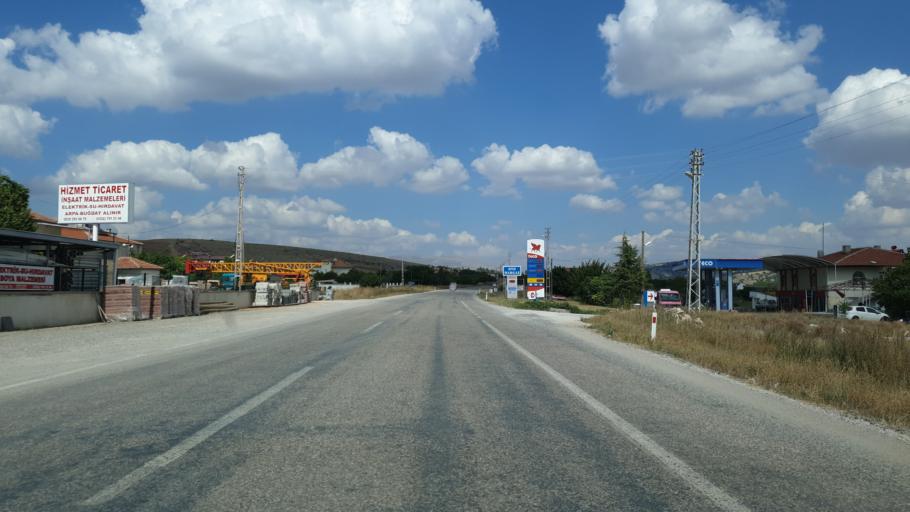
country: TR
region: Kayseri
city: Felahiye
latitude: 39.0998
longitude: 35.5857
